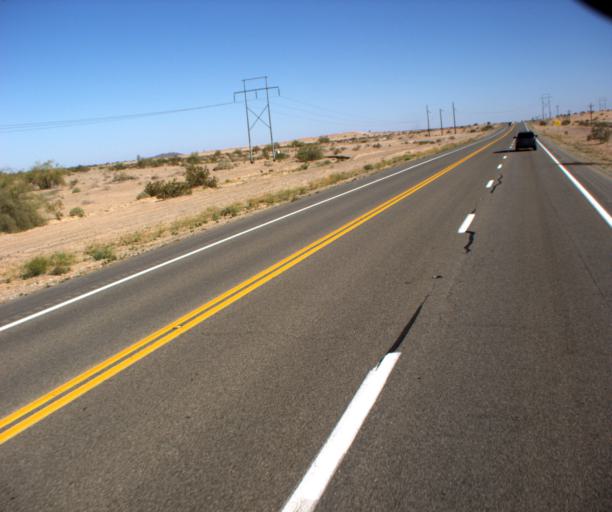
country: US
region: Arizona
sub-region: Yuma County
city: Fortuna Foothills
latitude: 32.8014
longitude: -114.3806
